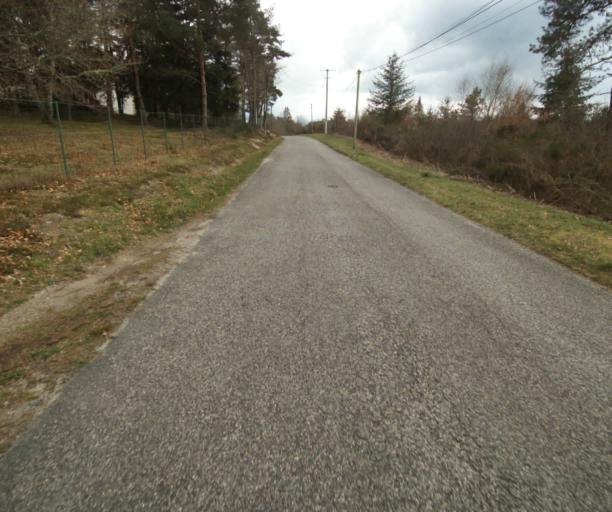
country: FR
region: Limousin
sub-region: Departement de la Correze
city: Correze
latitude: 45.2889
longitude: 1.9673
